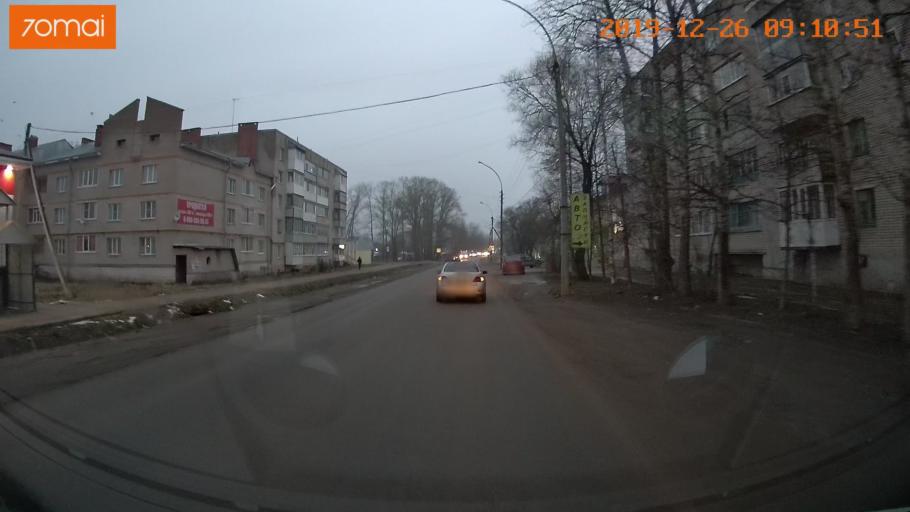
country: RU
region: Vologda
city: Gryazovets
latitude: 58.8732
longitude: 40.2525
